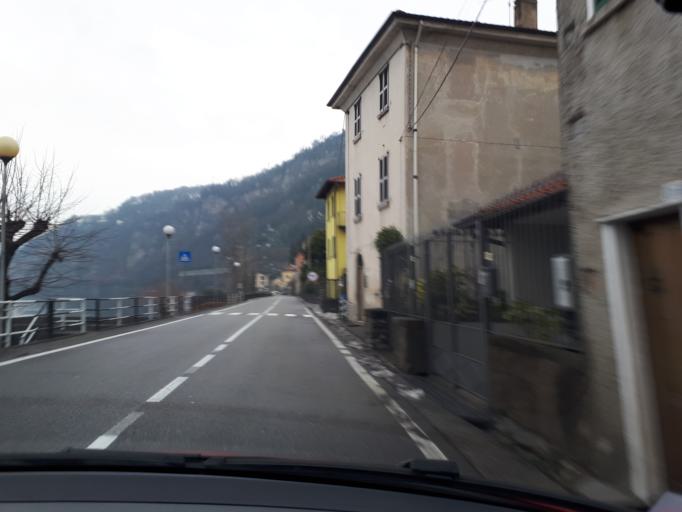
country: IT
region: Lombardy
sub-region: Provincia di Lecco
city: Mandello del Lario
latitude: 45.9367
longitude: 9.3128
